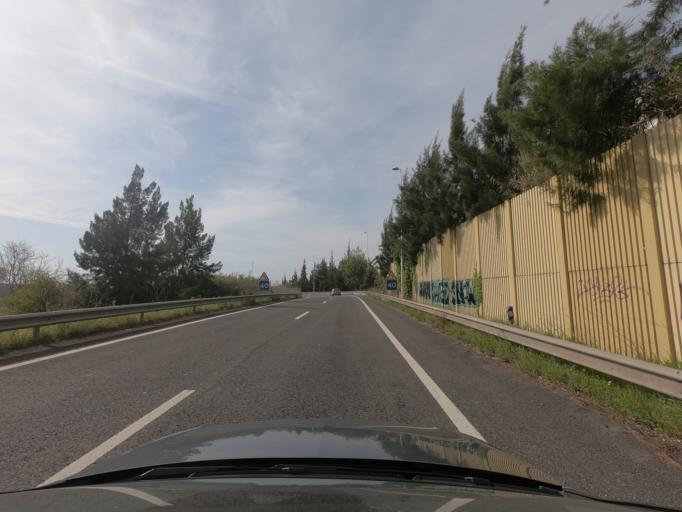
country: PT
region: Lisbon
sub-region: Loures
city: Moscavide
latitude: 38.7828
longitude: -9.1064
